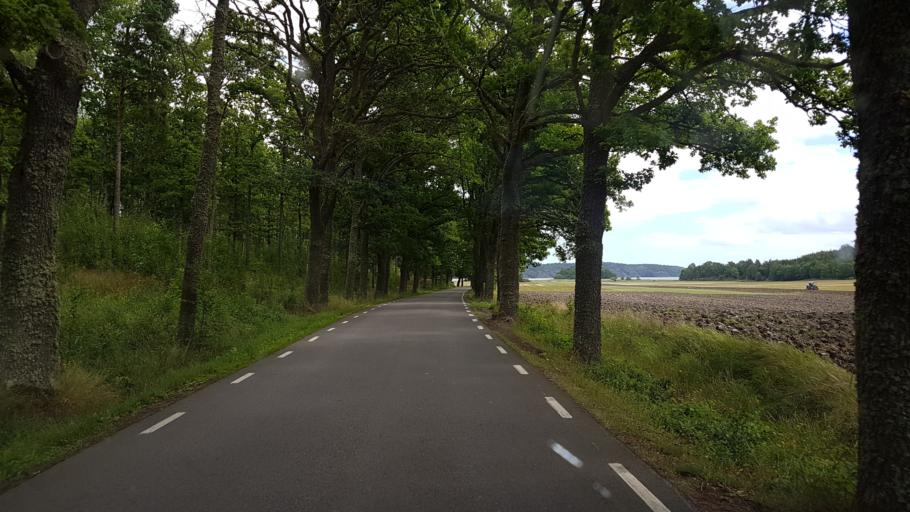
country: SE
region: OEstergoetland
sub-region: Valdemarsviks Kommun
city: Gusum
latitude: 58.4325
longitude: 16.5955
